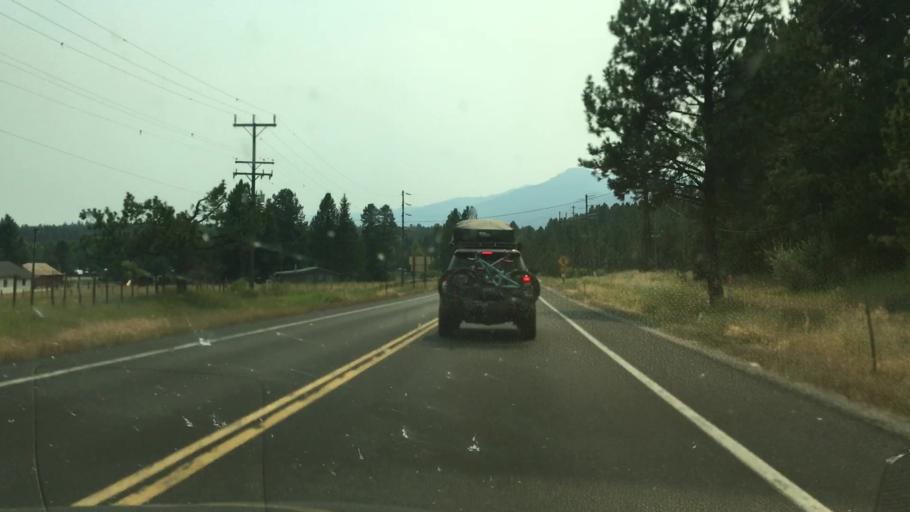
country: US
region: Idaho
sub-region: Valley County
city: Cascade
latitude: 44.5272
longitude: -116.0420
